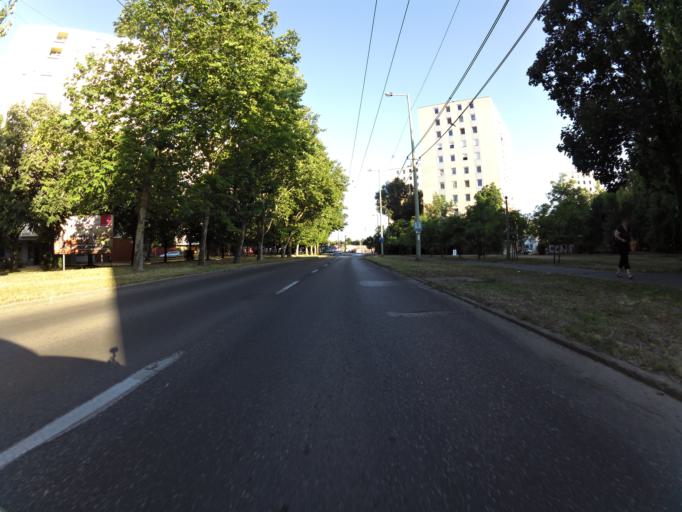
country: HU
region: Csongrad
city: Szeged
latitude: 46.2631
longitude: 20.1702
